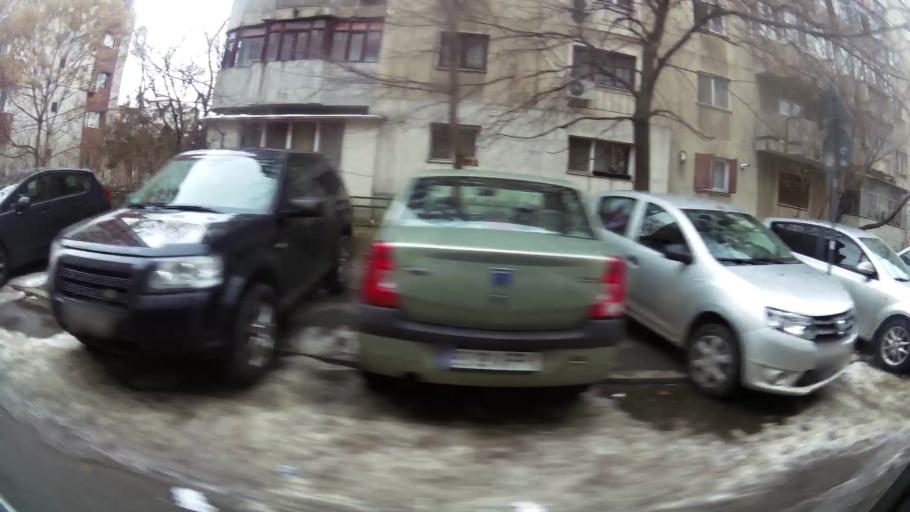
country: RO
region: Bucuresti
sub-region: Municipiul Bucuresti
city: Bucuresti
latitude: 44.4154
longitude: 26.0632
